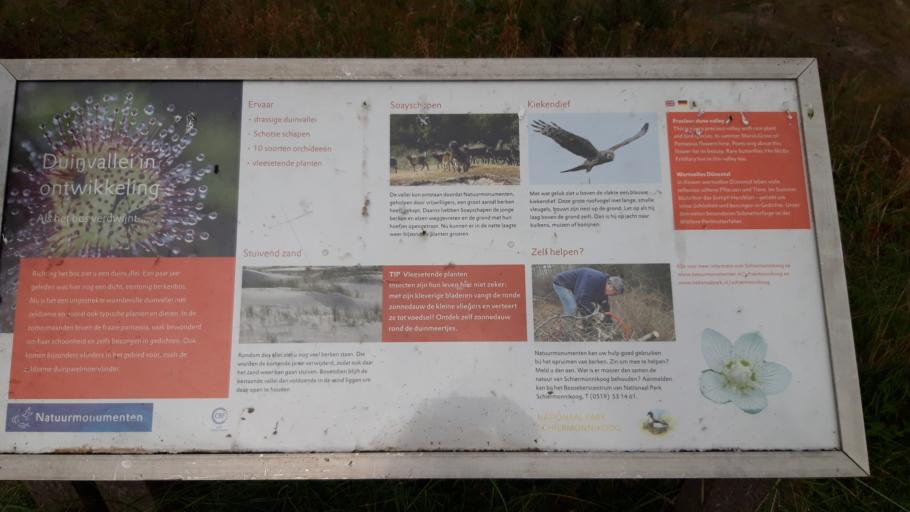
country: NL
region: Friesland
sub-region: Gemeente Schiermonnikoog
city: Schiermonnikoog
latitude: 53.4871
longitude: 6.1816
